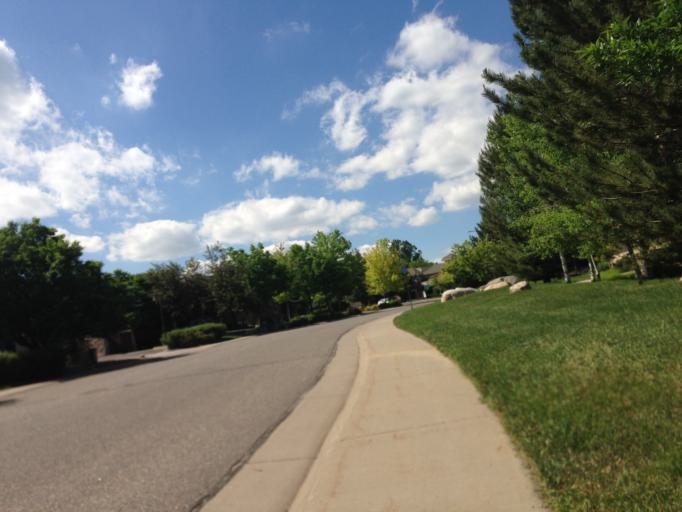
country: US
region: Colorado
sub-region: Boulder County
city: Louisville
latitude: 40.0118
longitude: -105.1283
